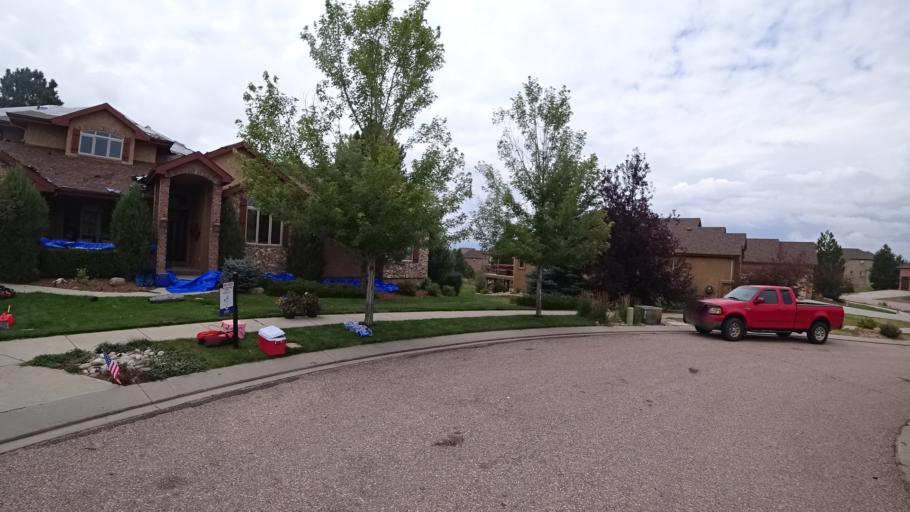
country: US
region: Colorado
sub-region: El Paso County
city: Gleneagle
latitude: 39.0157
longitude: -104.7955
